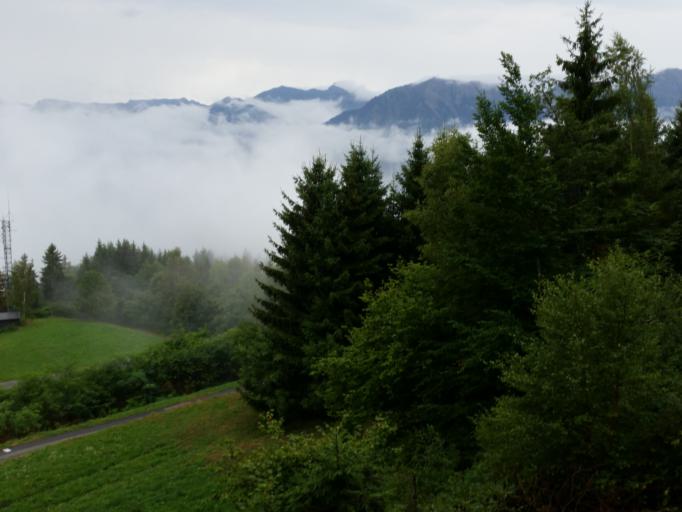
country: FR
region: Rhone-Alpes
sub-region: Departement de la Savoie
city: Albertville
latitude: 45.6778
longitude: 6.4262
